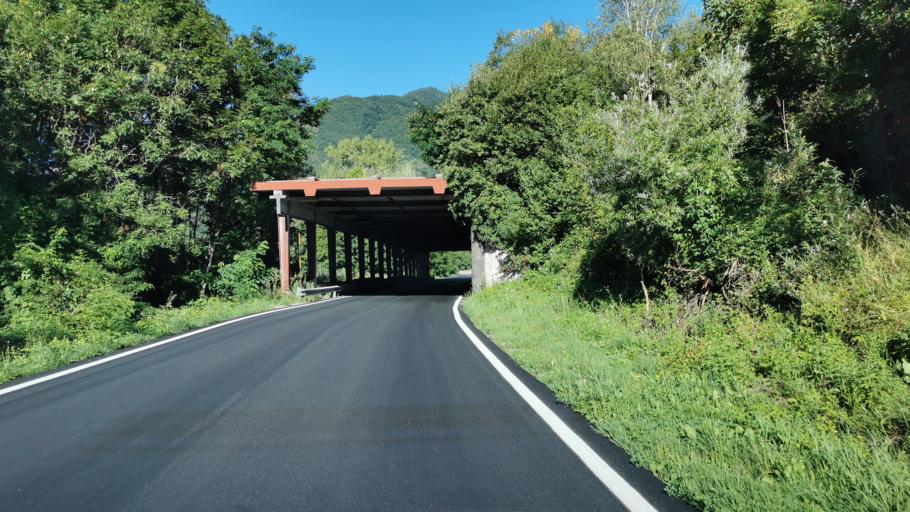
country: IT
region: Piedmont
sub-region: Provincia di Cuneo
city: Valdieri
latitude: 44.2612
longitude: 7.3658
